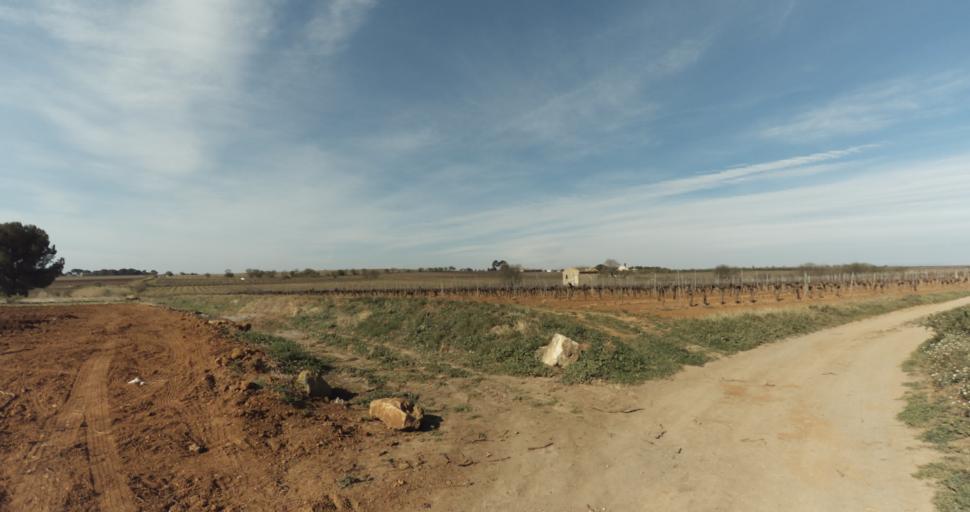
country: FR
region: Languedoc-Roussillon
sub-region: Departement de l'Herault
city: Marseillan
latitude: 43.3518
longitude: 3.4959
